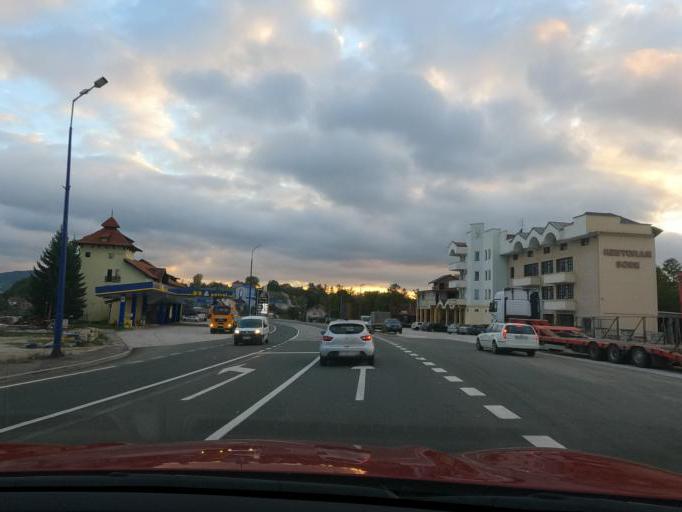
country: RS
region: Central Serbia
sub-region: Zlatiborski Okrug
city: Uzice
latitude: 43.8111
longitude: 19.7928
